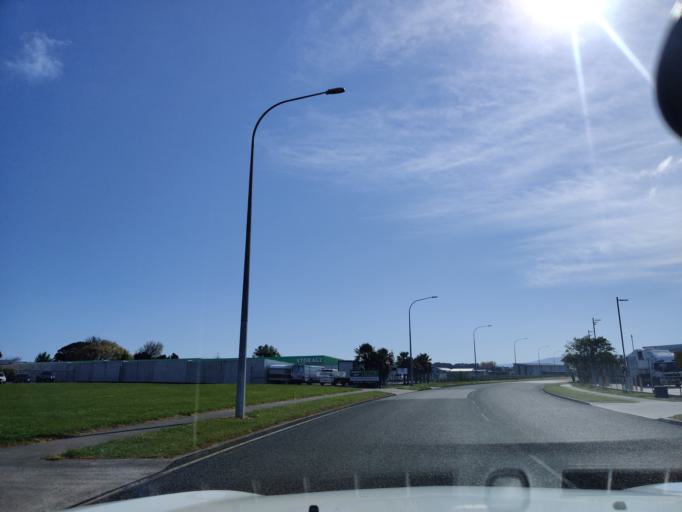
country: NZ
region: Manawatu-Wanganui
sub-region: Palmerston North City
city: Palmerston North
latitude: -40.3340
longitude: 175.6452
